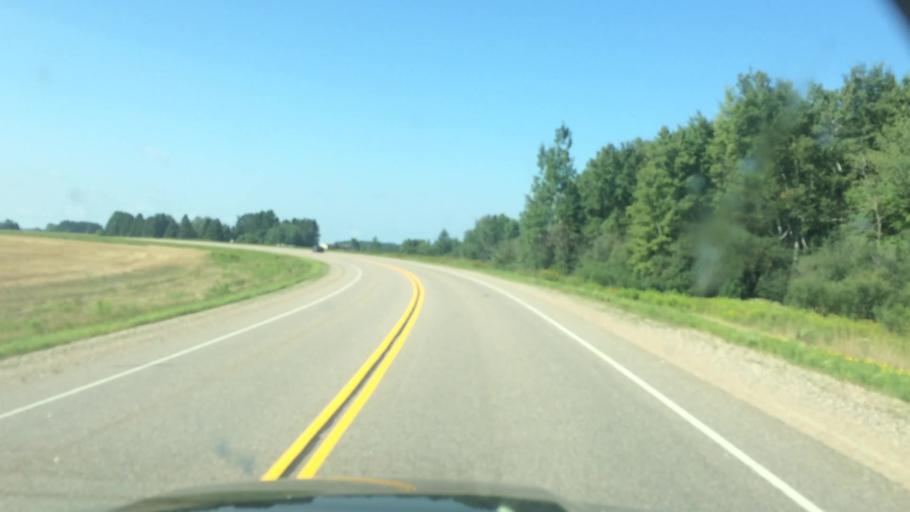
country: US
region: Wisconsin
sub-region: Langlade County
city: Antigo
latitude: 45.1514
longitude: -89.1830
